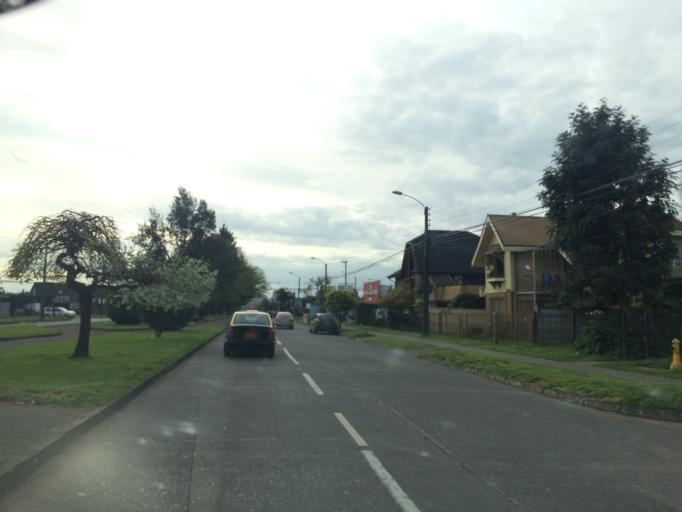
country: CL
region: Araucania
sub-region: Provincia de Cautin
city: Temuco
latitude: -38.7393
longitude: -72.6248
